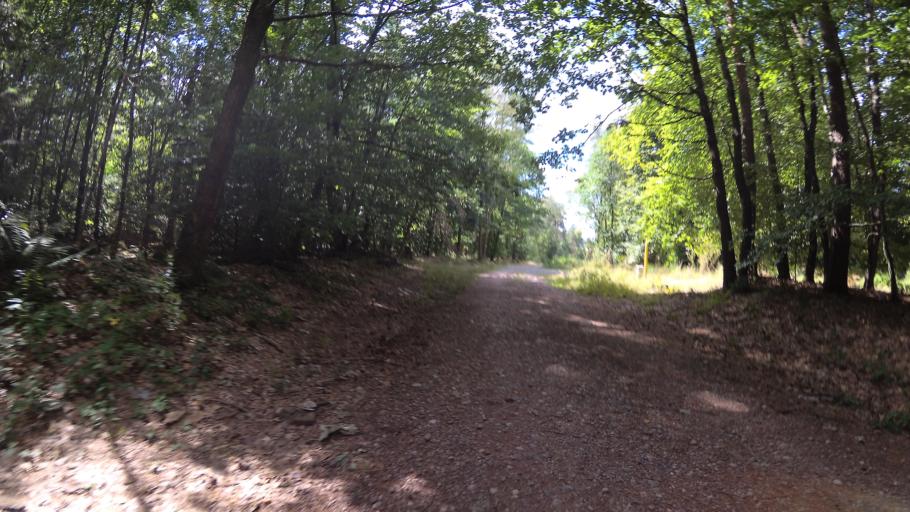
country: DE
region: Saarland
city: Homburg
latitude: 49.3285
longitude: 7.3020
